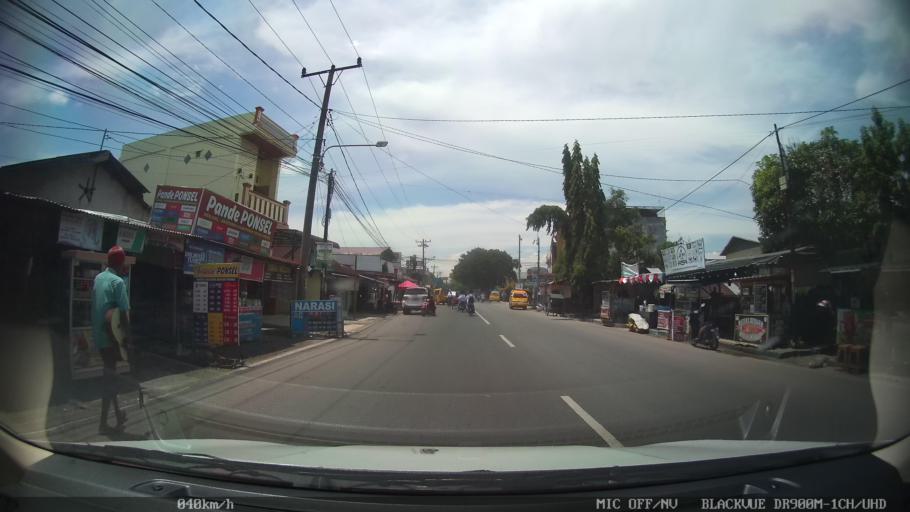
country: ID
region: North Sumatra
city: Binjai
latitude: 3.5947
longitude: 98.4905
